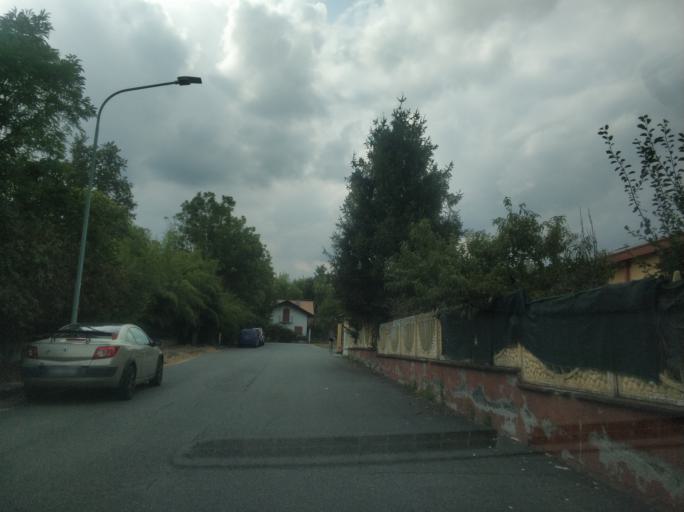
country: IT
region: Piedmont
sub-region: Provincia di Torino
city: Barbania
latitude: 45.2927
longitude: 7.6499
